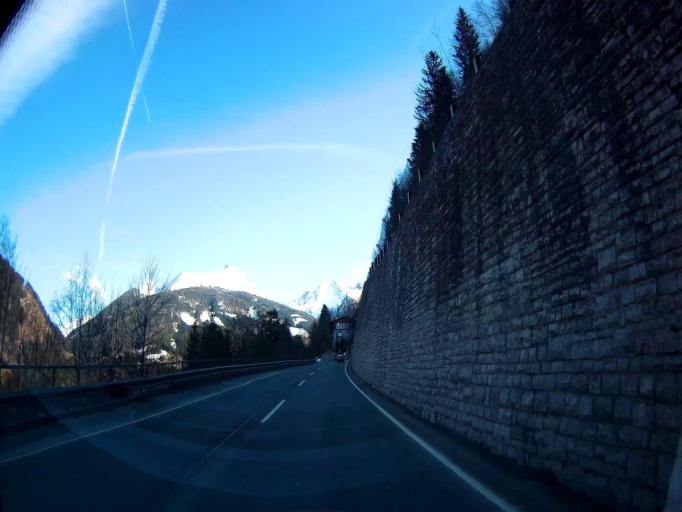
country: AT
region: Salzburg
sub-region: Politischer Bezirk Sankt Johann im Pongau
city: Bad Gastein
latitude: 47.1360
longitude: 13.1263
